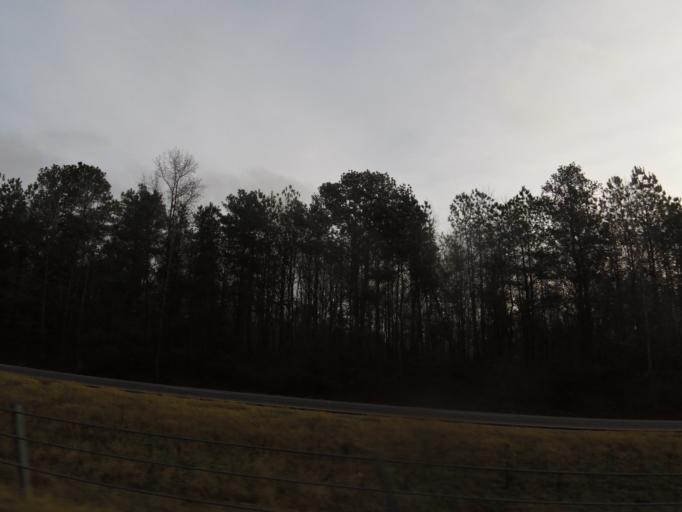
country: US
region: Alabama
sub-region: Autauga County
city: Marbury
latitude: 32.7167
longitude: -86.5303
